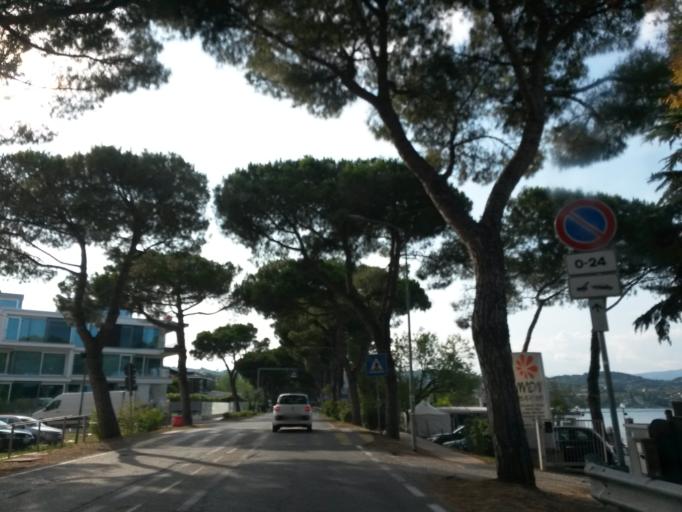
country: IT
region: Lombardy
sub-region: Provincia di Brescia
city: Padenghe sul Garda
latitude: 45.4901
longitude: 10.5233
